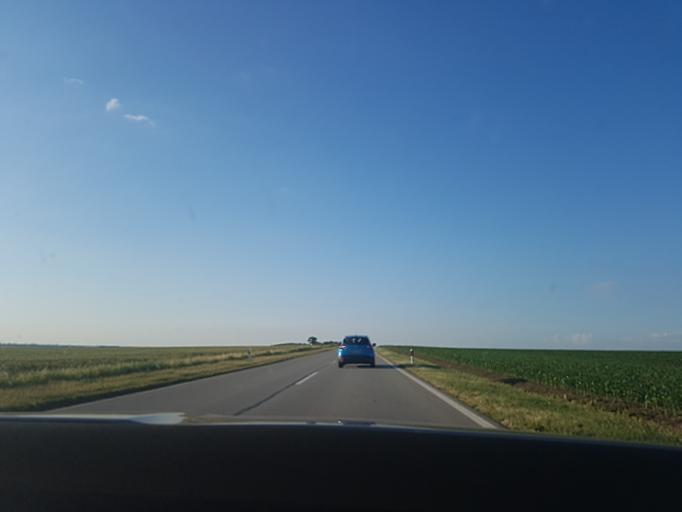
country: RO
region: Timis
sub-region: Comuna Moravita
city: Moravita
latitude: 45.1922
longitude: 21.2989
